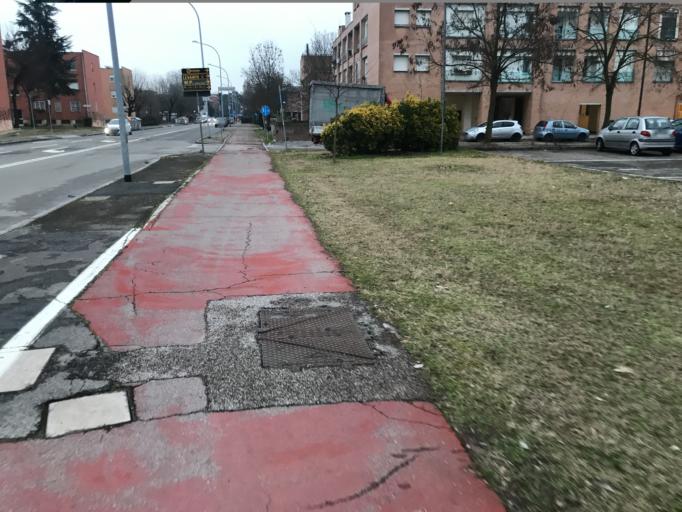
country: IT
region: Emilia-Romagna
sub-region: Provincia di Bologna
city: Progresso
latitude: 44.5369
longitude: 11.3510
